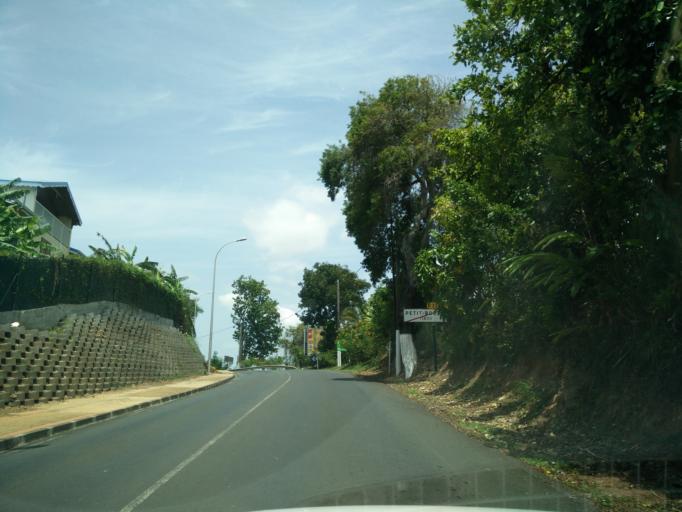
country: GP
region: Guadeloupe
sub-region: Guadeloupe
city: Petit-Bourg
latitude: 16.1972
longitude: -61.5965
